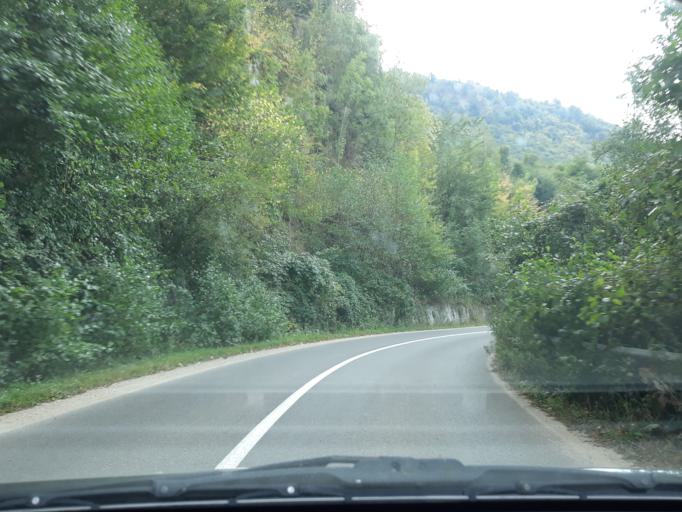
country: RO
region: Bihor
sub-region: Comuna Pietroasa
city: Pietroasa
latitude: 46.5888
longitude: 22.5805
